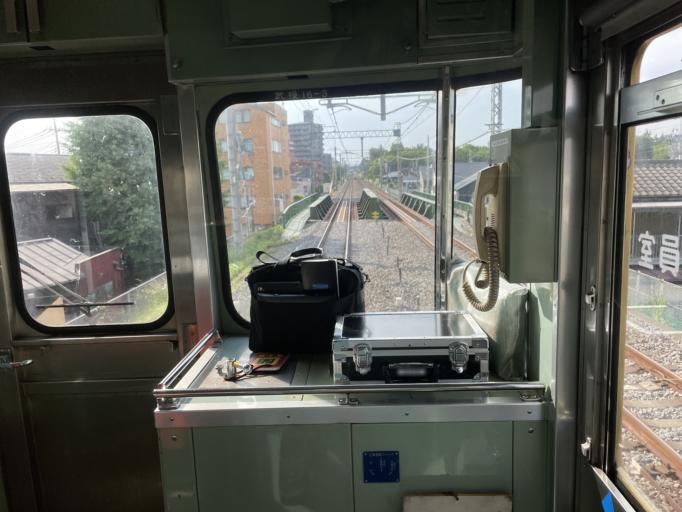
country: JP
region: Saitama
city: Tokorozawa
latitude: 35.7930
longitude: 139.4717
